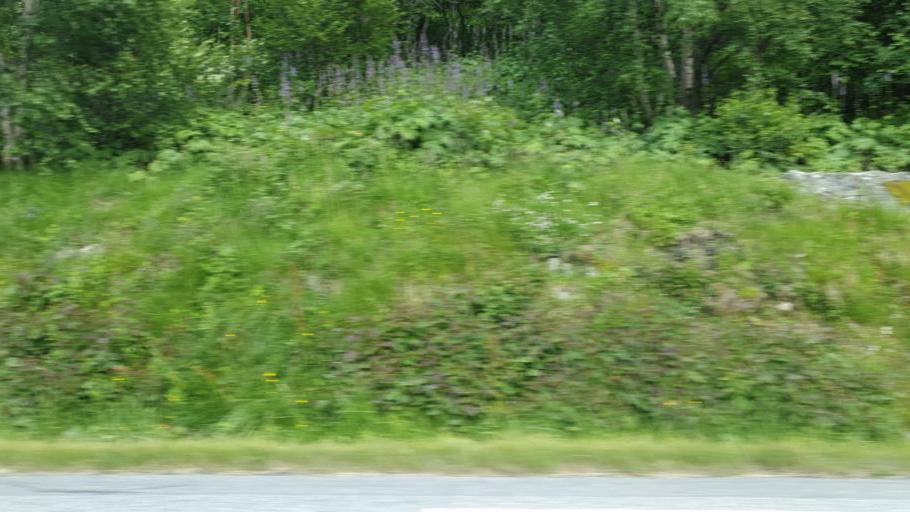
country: NO
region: Oppland
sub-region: Vaga
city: Vagamo
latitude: 61.8310
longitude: 8.9623
